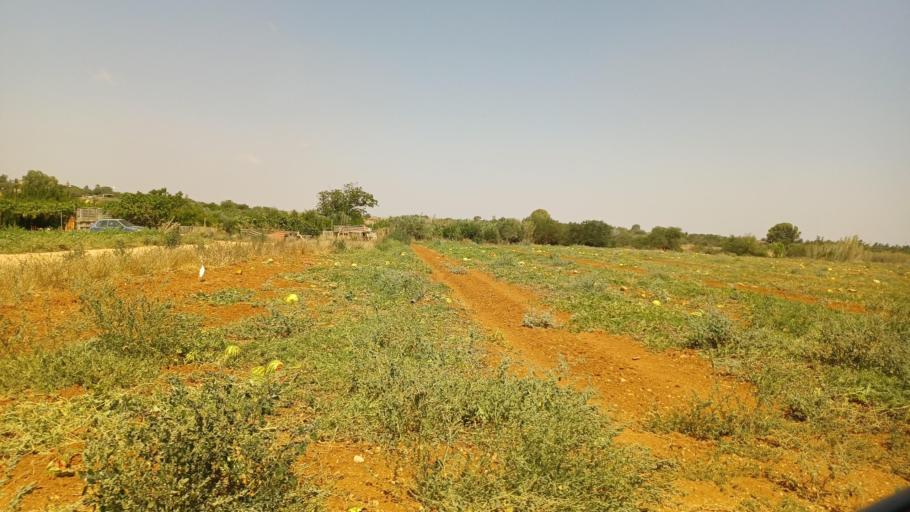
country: CY
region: Ammochostos
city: Frenaros
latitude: 35.0617
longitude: 33.9199
